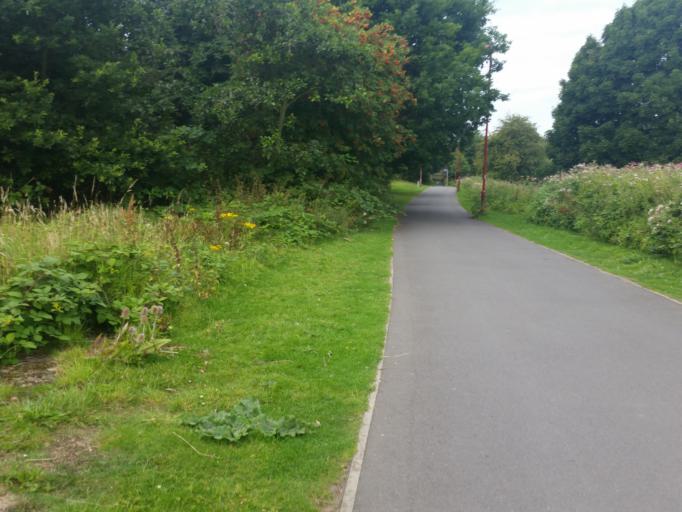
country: GB
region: England
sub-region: Derby
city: Derby
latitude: 52.9185
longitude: -1.4606
